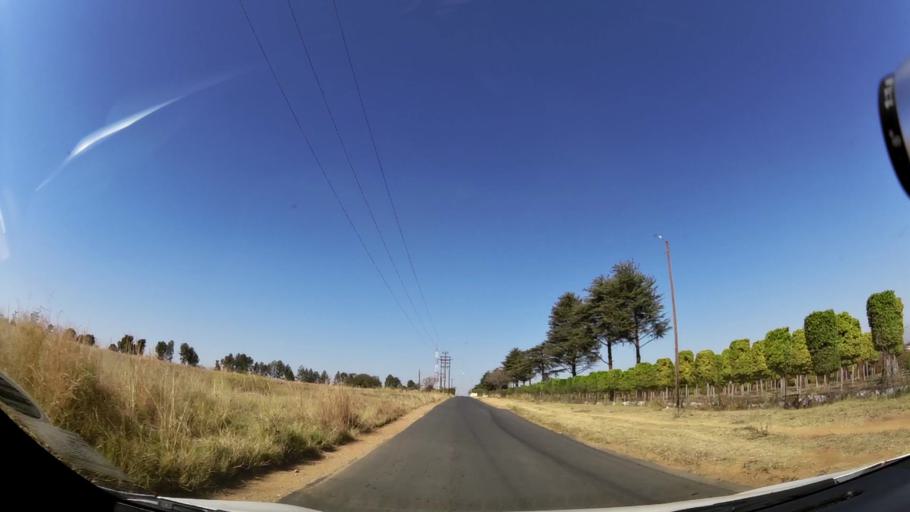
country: ZA
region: Gauteng
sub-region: City of Johannesburg Metropolitan Municipality
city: Diepsloot
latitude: -25.9214
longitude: 28.0740
